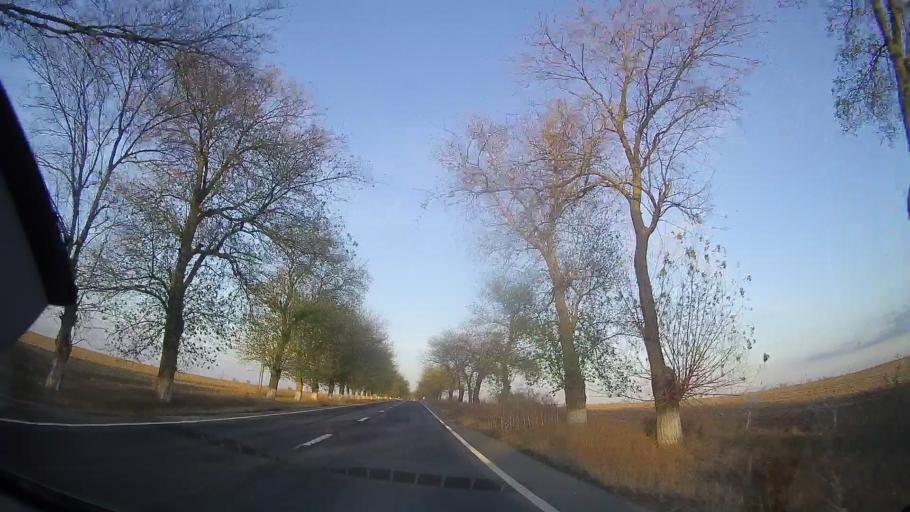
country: RO
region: Constanta
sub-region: Comuna Comana
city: Comana
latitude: 43.8983
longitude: 28.3221
